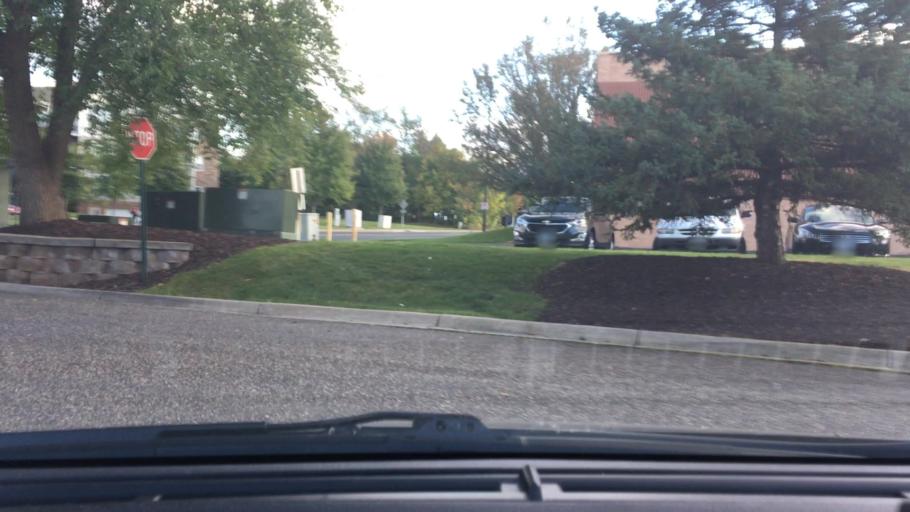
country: US
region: Minnesota
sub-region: Hennepin County
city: Maple Grove
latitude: 45.0666
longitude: -93.4400
